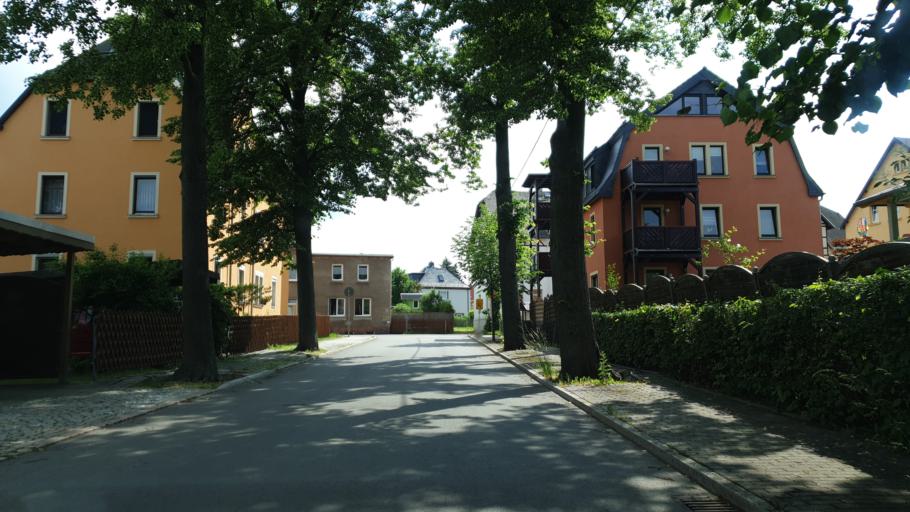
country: DE
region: Saxony
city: Lugau
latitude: 50.7337
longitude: 12.7386
